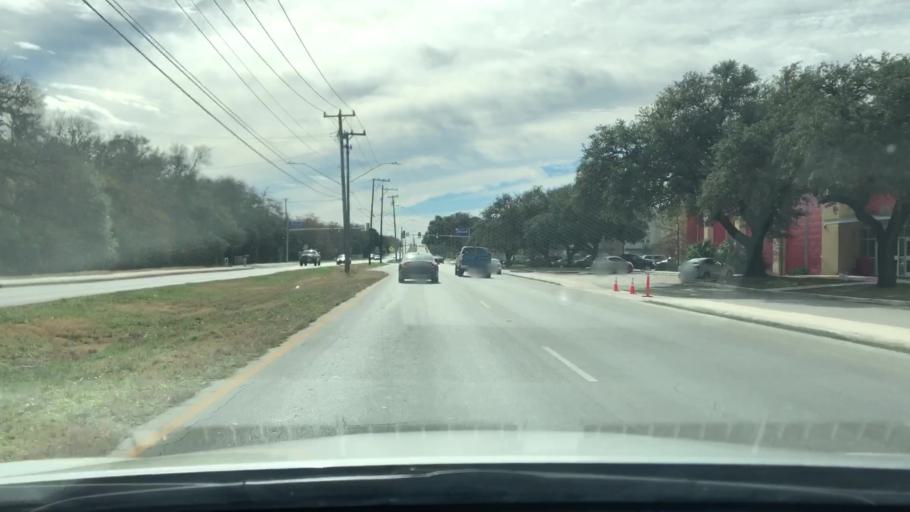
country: US
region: Texas
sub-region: Bexar County
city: Terrell Hills
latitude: 29.5069
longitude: -98.4346
